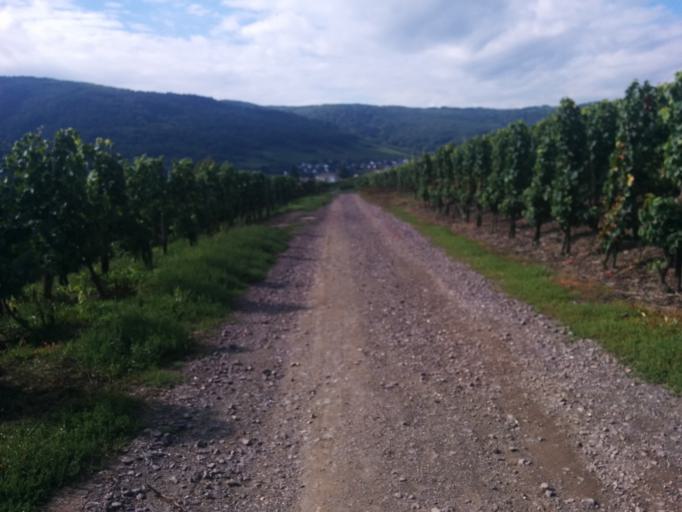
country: DE
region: Rheinland-Pfalz
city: Monzelfeld
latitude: 49.9147
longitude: 7.0606
